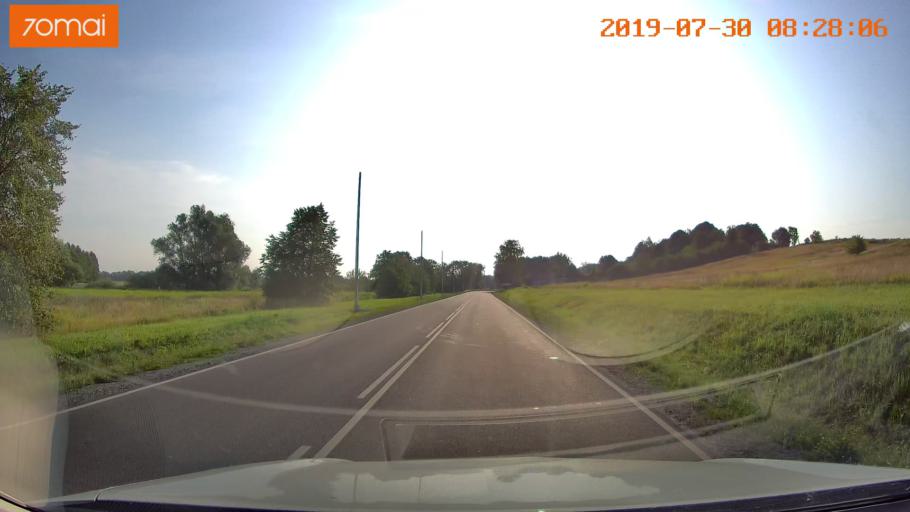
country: RU
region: Kaliningrad
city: Chernyakhovsk
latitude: 54.6290
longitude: 21.6397
